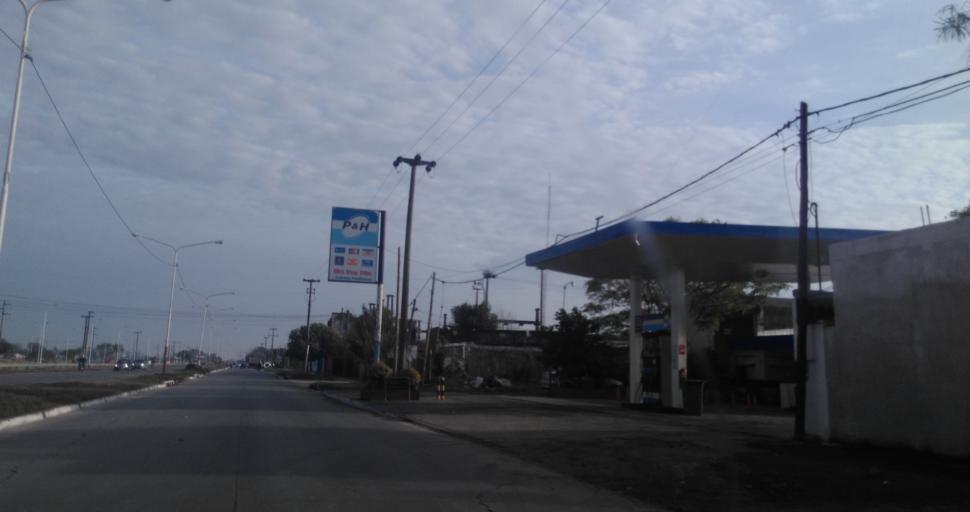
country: AR
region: Chaco
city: Resistencia
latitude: -27.4739
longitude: -59.0039
